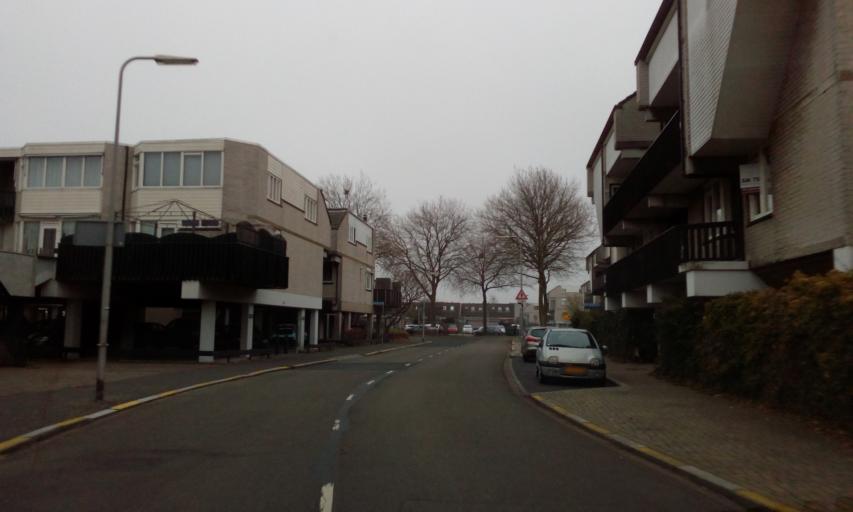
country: NL
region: South Holland
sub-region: Gemeente Capelle aan den IJssel
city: Capelle aan den IJssel
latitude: 51.9495
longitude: 4.5729
